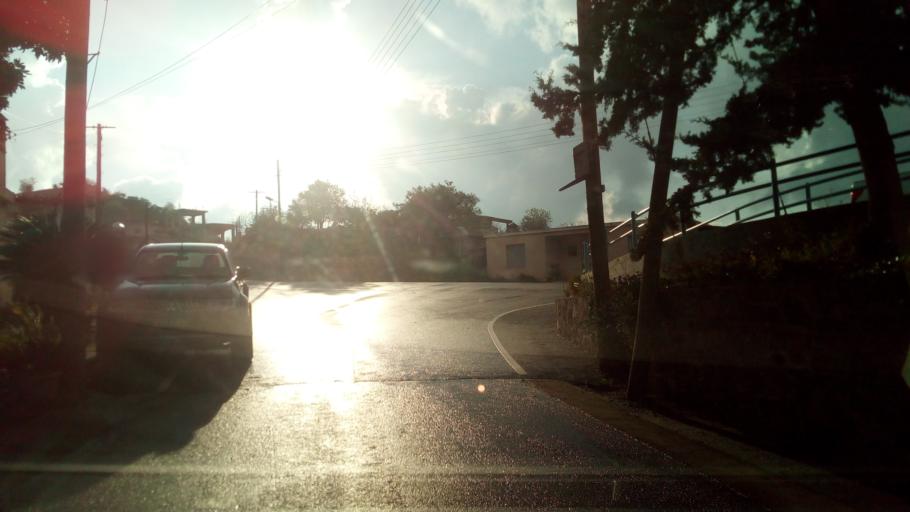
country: CY
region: Lefkosia
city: Kato Pyrgos
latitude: 35.1716
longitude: 32.6577
